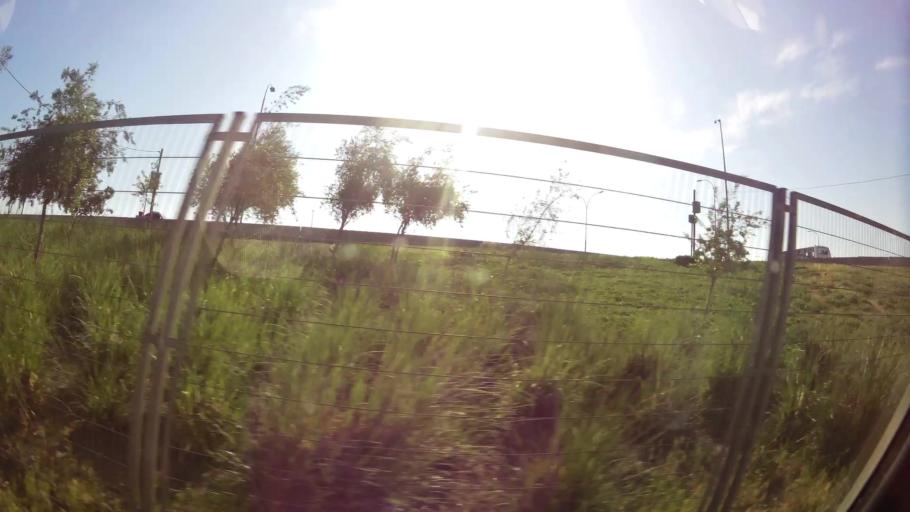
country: CL
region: Santiago Metropolitan
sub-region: Provincia de Santiago
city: Santiago
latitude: -33.4792
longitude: -70.6848
